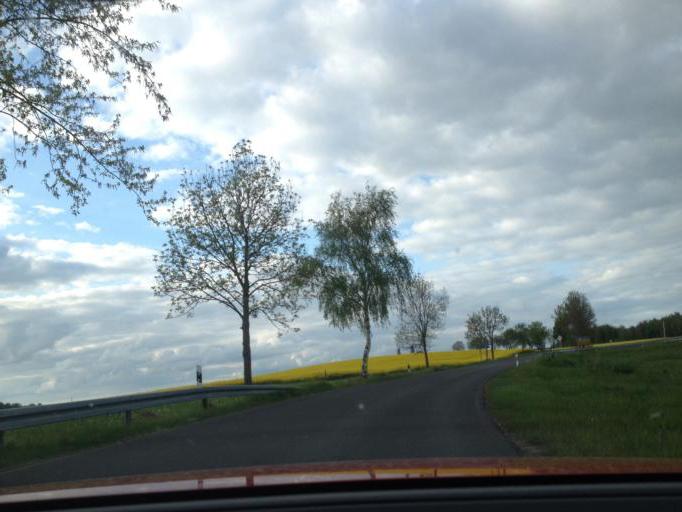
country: DE
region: Bavaria
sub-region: Upper Franconia
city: Arzberg
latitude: 50.0472
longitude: 12.1659
